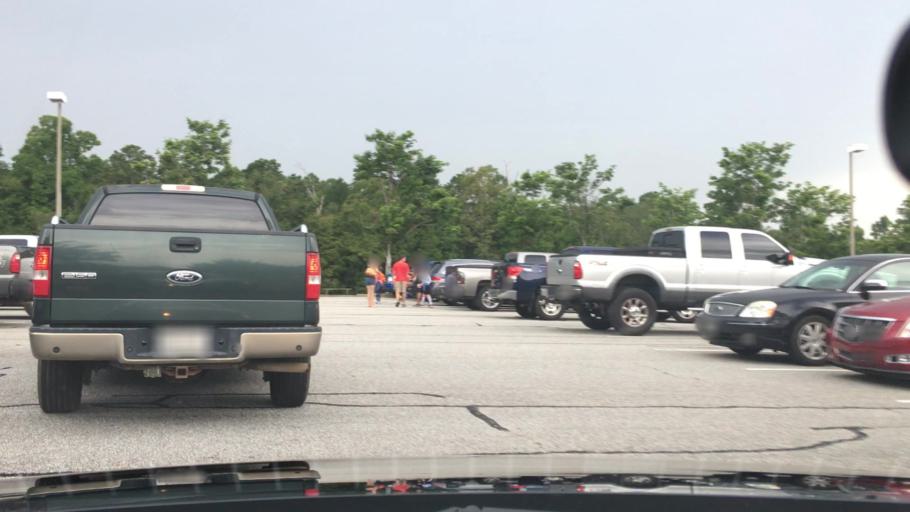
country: US
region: Georgia
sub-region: Coweta County
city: East Newnan
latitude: 33.3375
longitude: -84.6911
